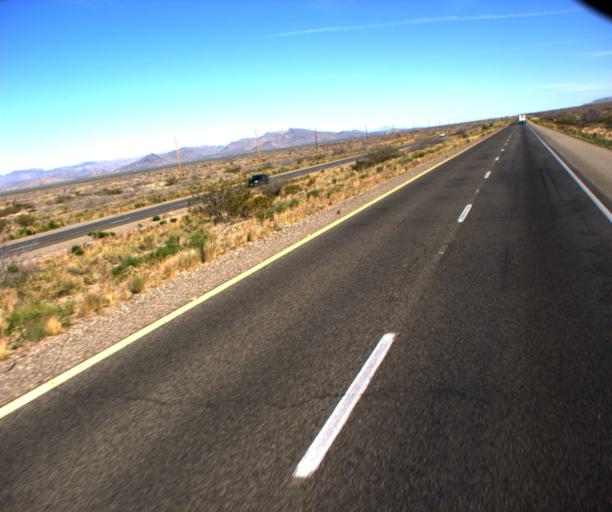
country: US
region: Arizona
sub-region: Mohave County
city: Golden Valley
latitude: 35.2740
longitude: -114.1701
